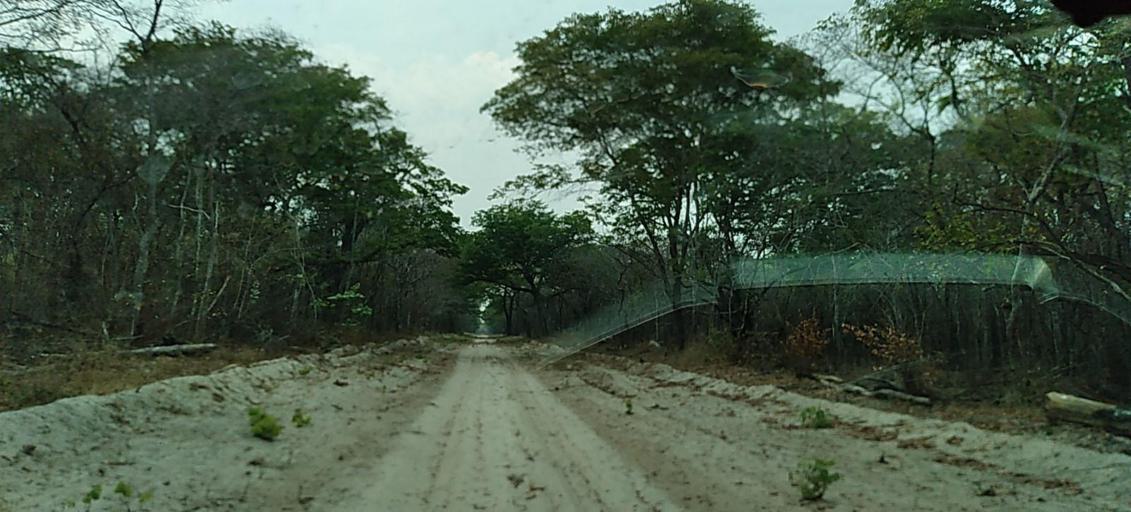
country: ZM
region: Western
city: Lukulu
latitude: -14.0144
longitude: 23.5805
